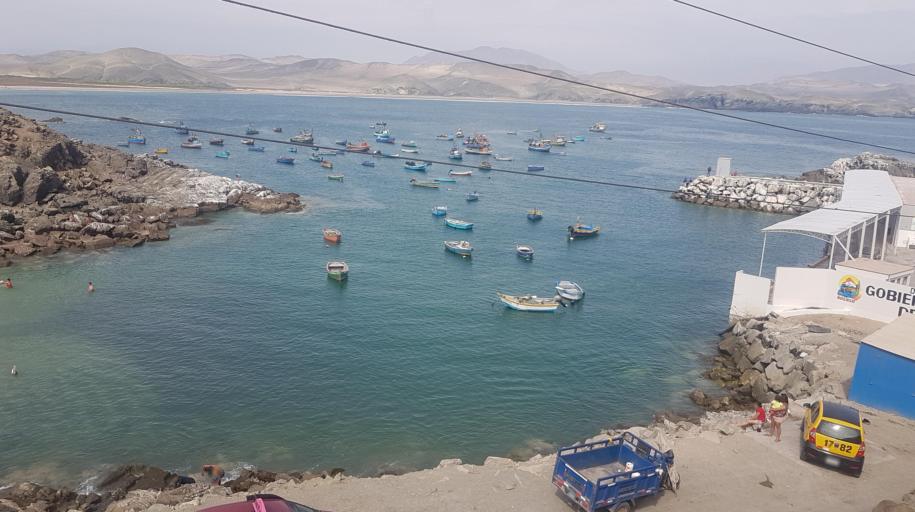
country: PE
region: Ancash
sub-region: Provincia de Santa
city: Samanco
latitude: -9.3283
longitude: -78.4733
